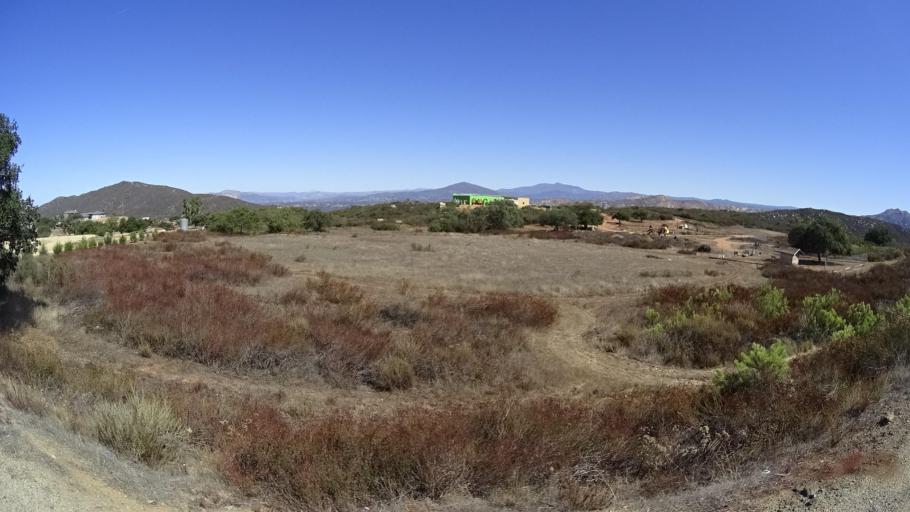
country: US
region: California
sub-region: San Diego County
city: Jamul
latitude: 32.7322
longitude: -116.7960
